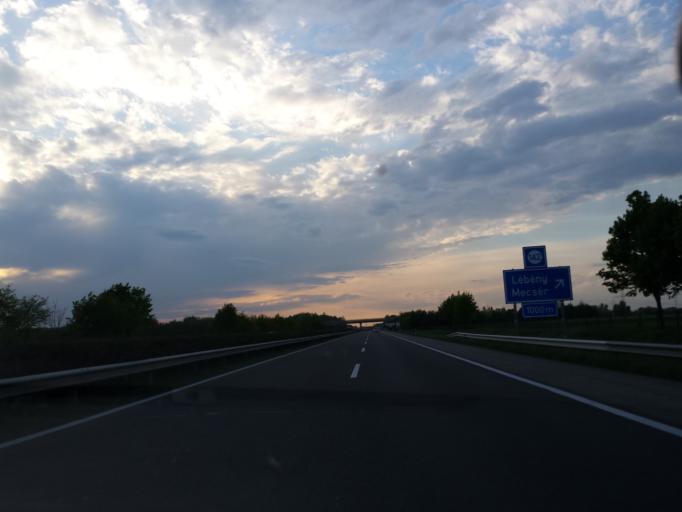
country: HU
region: Gyor-Moson-Sopron
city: Mosonszentmiklos
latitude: 47.7407
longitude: 17.4309
